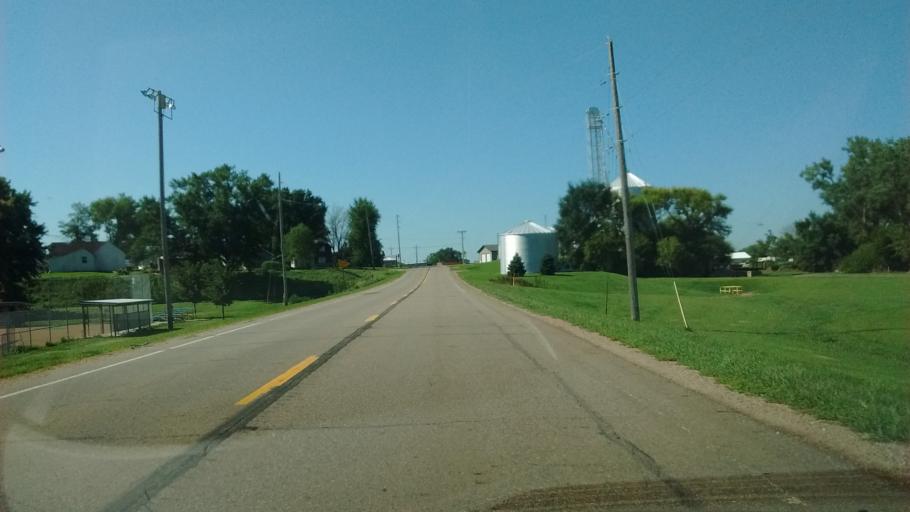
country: US
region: Iowa
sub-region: Woodbury County
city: Moville
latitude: 42.4918
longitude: -96.0739
